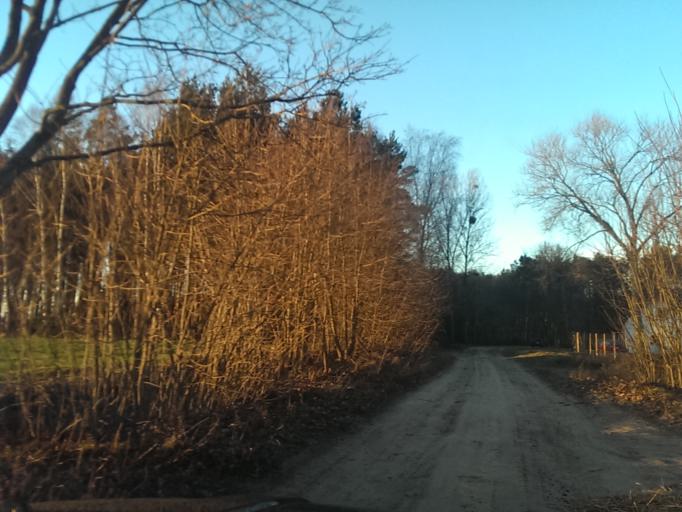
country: PL
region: Kujawsko-Pomorskie
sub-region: Powiat nakielski
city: Szubin
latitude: 53.0607
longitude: 17.6848
